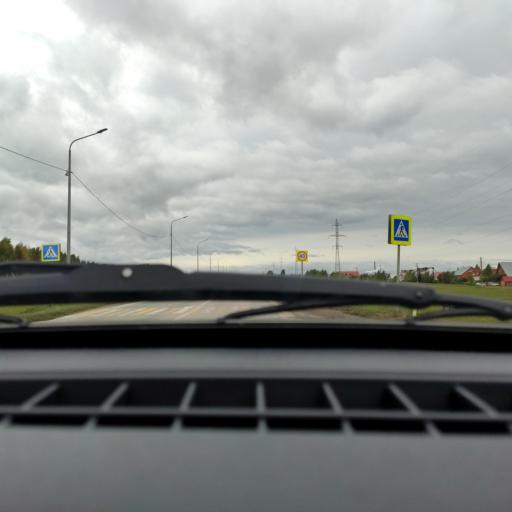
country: RU
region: Bashkortostan
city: Rayevskiy
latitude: 54.0571
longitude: 54.9125
